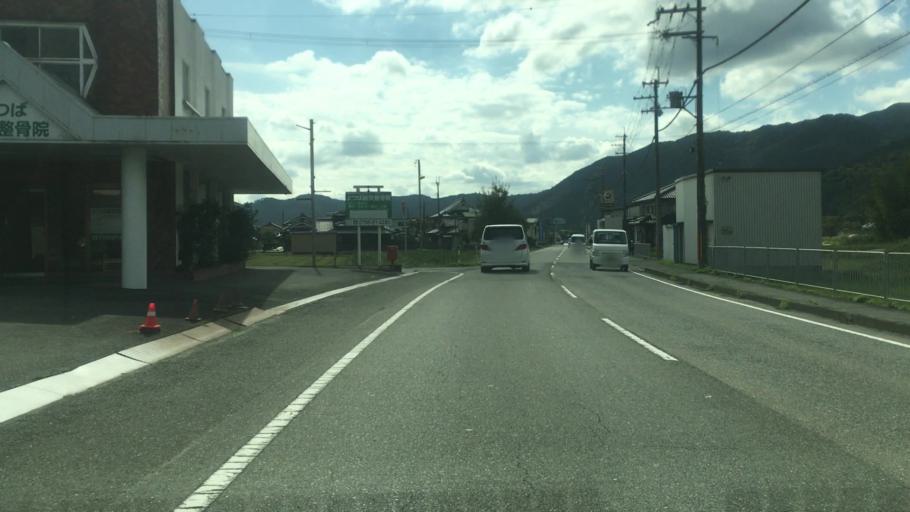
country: JP
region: Kyoto
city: Fukuchiyama
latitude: 35.2473
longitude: 135.0063
